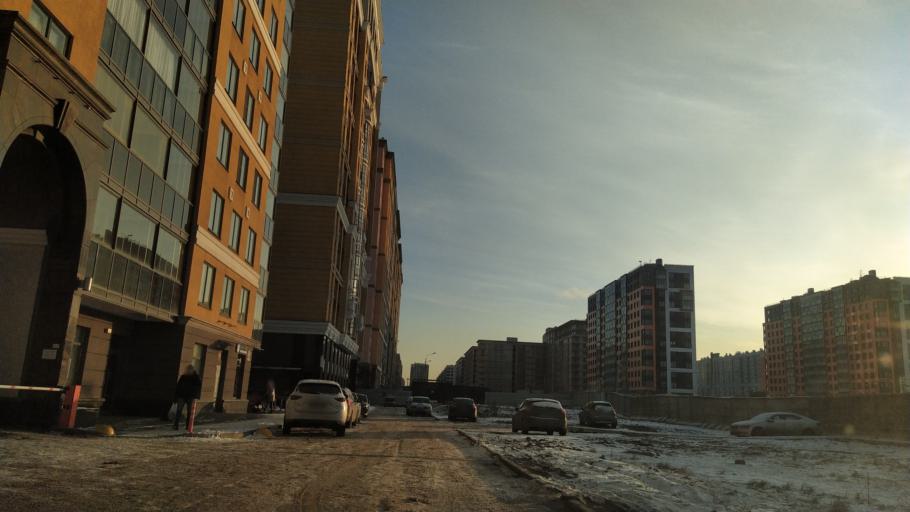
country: RU
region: St.-Petersburg
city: Admiralteisky
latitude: 59.9069
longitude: 30.3121
